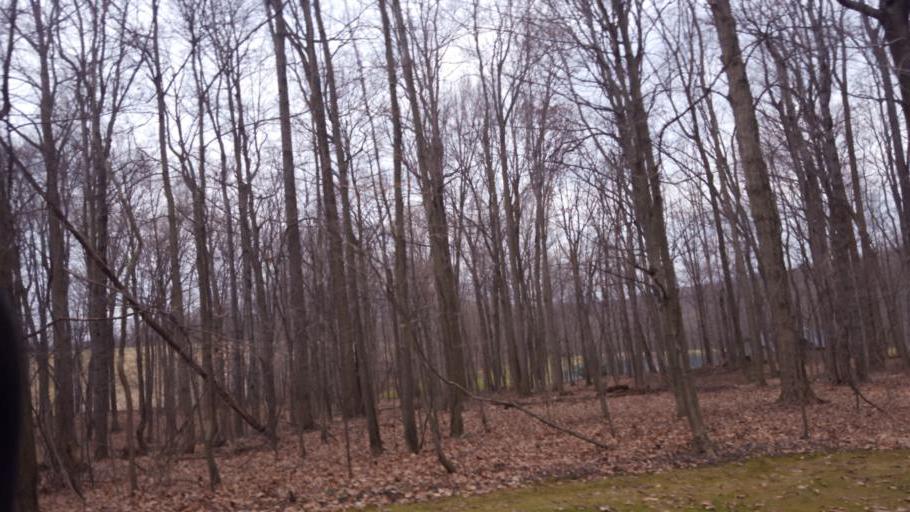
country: US
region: Ohio
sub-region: Ashland County
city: Loudonville
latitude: 40.6906
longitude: -82.2550
